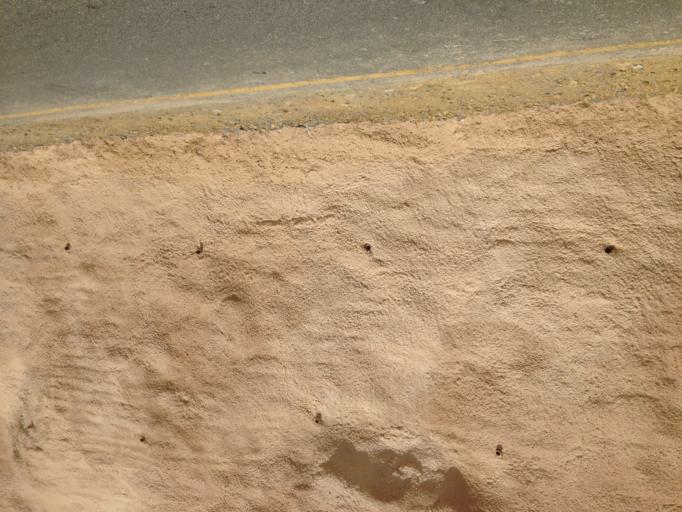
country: OM
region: Ash Sharqiyah
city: Ibra'
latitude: 23.0871
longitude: 58.8483
